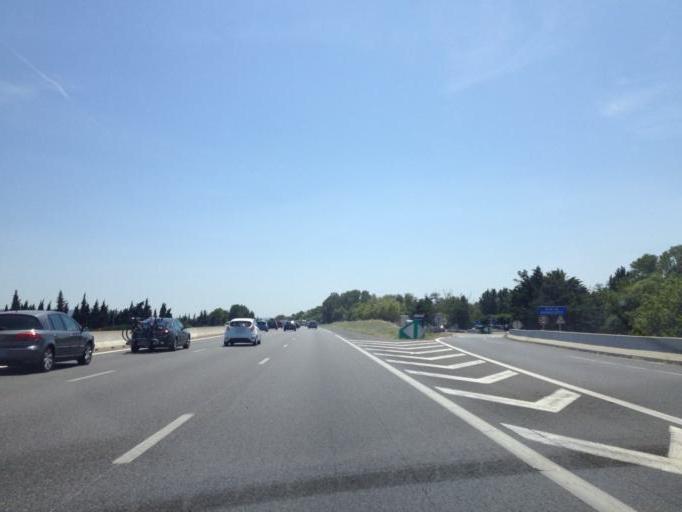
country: FR
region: Rhone-Alpes
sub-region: Departement de la Drome
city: La Garde-Adhemar
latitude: 44.4049
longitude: 4.7291
